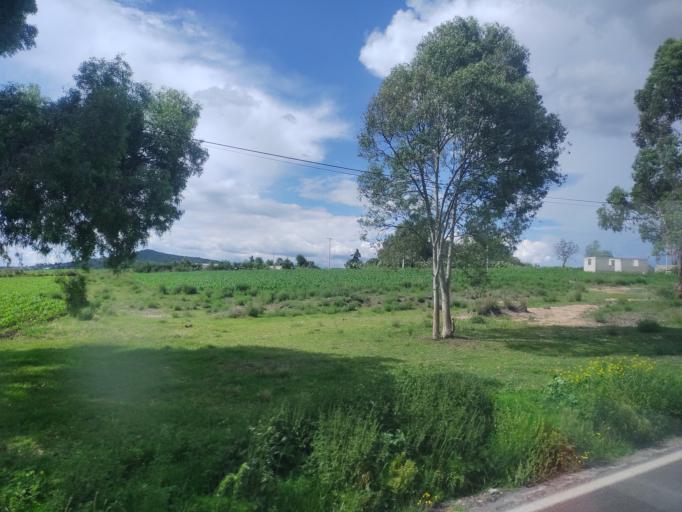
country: MX
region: Mexico
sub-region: Aculco
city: El Colorado
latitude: 20.0959
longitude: -99.7529
